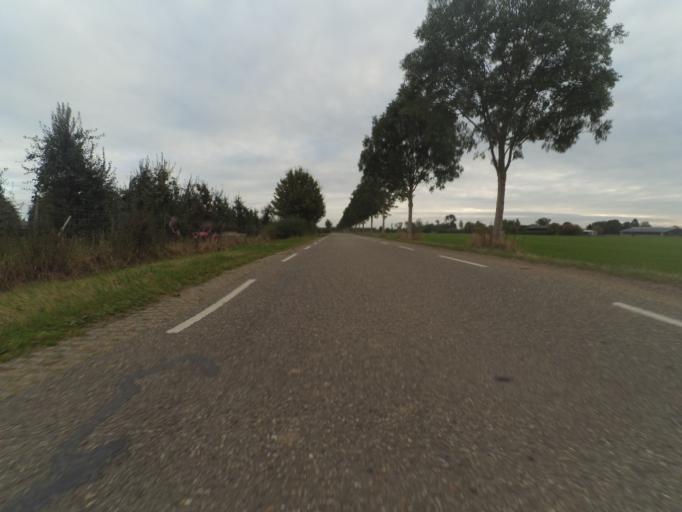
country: NL
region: Utrecht
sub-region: Gemeente Wijk bij Duurstede
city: Wijk bij Duurstede
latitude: 51.9918
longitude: 5.3332
